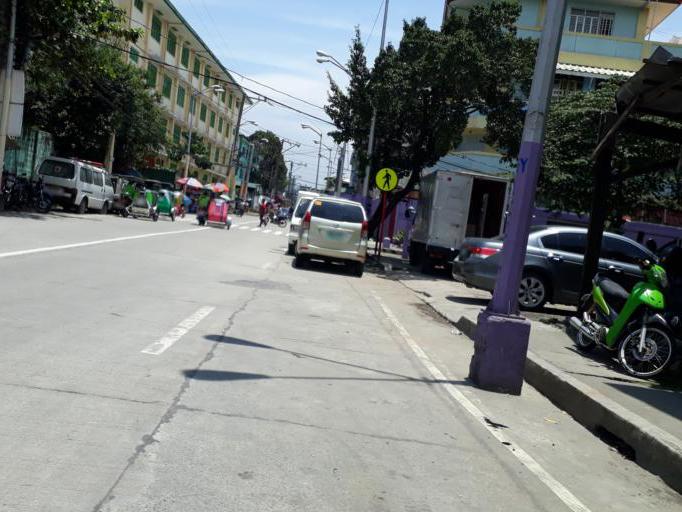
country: PH
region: Calabarzon
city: Del Monte
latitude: 14.6471
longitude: 120.9917
